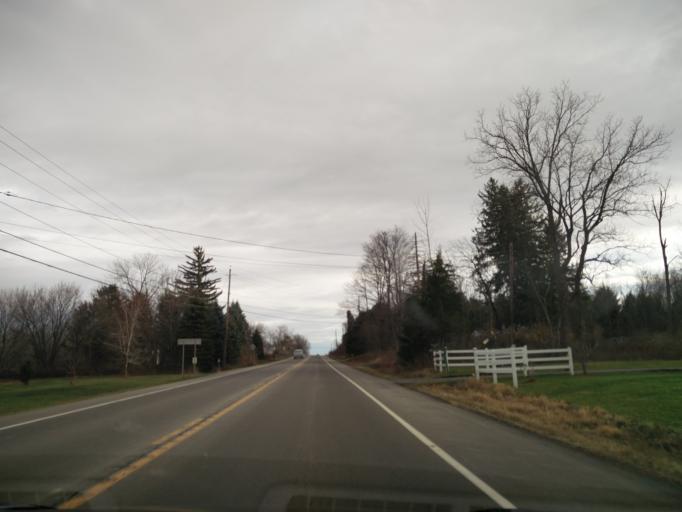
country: US
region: New York
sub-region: Tompkins County
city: Trumansburg
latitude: 42.5040
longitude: -76.6090
